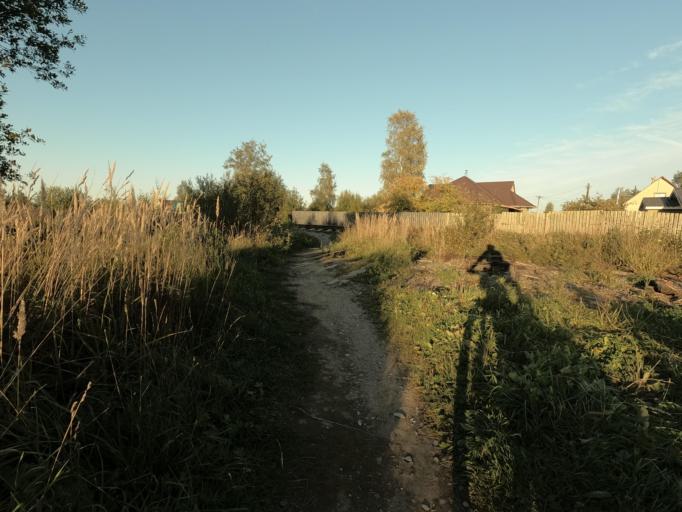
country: RU
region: Leningrad
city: Nikol'skoye
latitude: 59.7055
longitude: 30.7965
